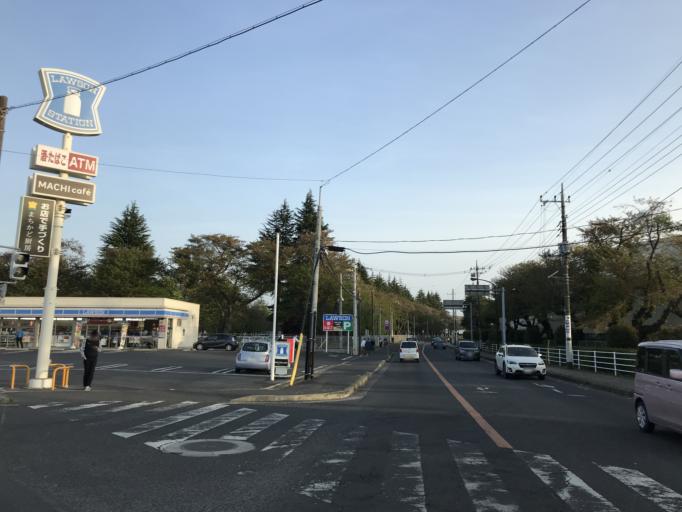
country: JP
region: Ibaraki
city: Katsuta
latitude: 36.3860
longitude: 140.5275
